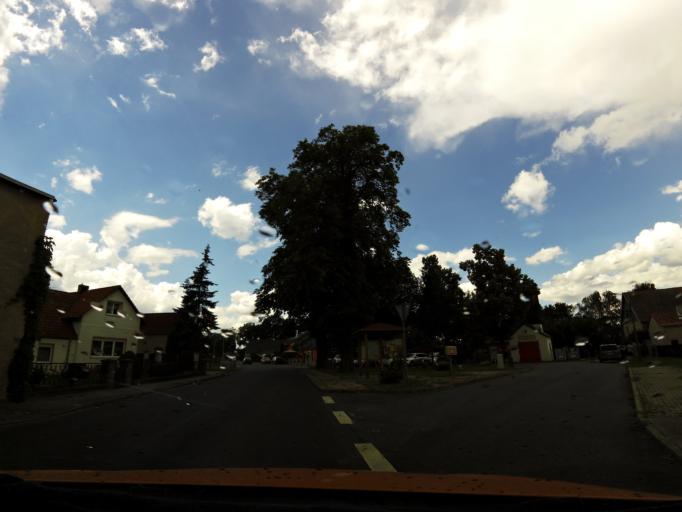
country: DE
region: Brandenburg
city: Munchehofe
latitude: 52.2180
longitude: 13.8299
